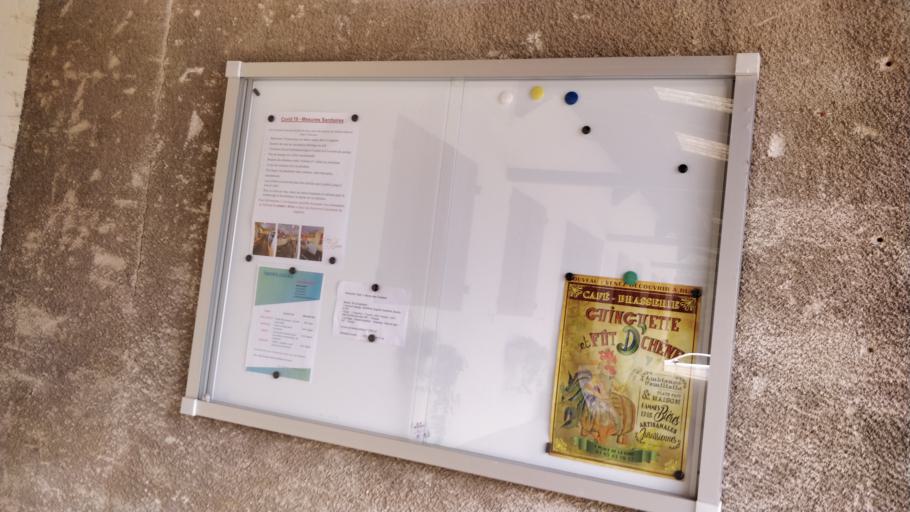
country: FR
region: Bourgogne
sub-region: Departement de Saone-et-Loire
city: Buxy
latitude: 46.7310
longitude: 4.6864
